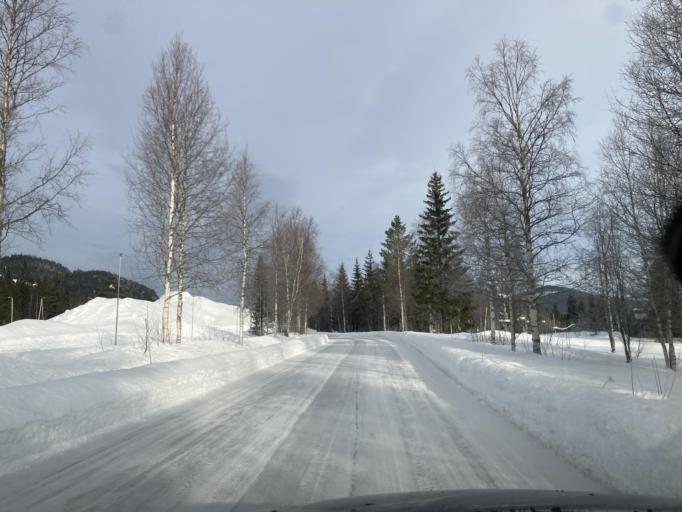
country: NO
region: Hedmark
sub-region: Trysil
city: Innbygda
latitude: 61.3006
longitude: 12.2451
